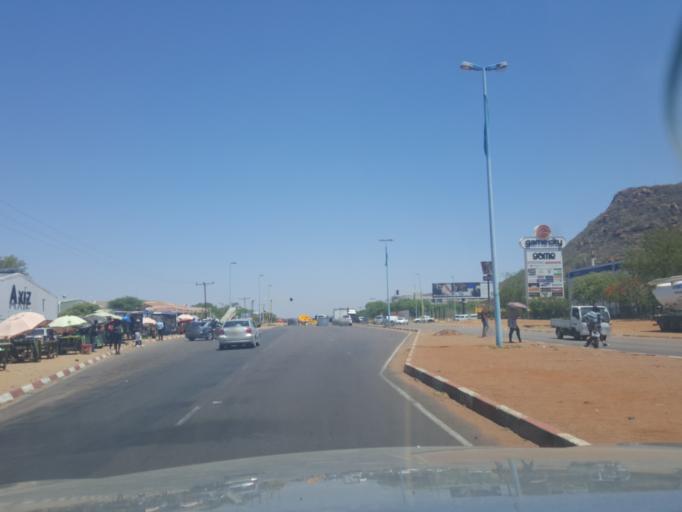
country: BW
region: South East
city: Gaborone
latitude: -24.6888
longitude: 25.8823
